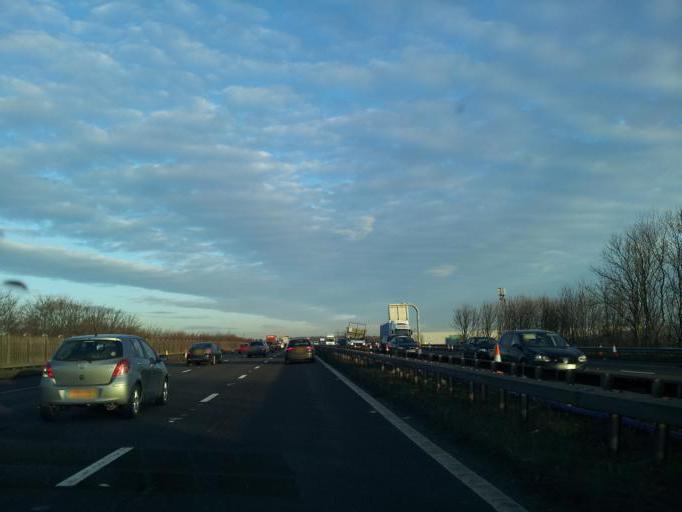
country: GB
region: England
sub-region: City and Borough of Wakefield
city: Normanton
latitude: 53.7140
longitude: -1.4191
